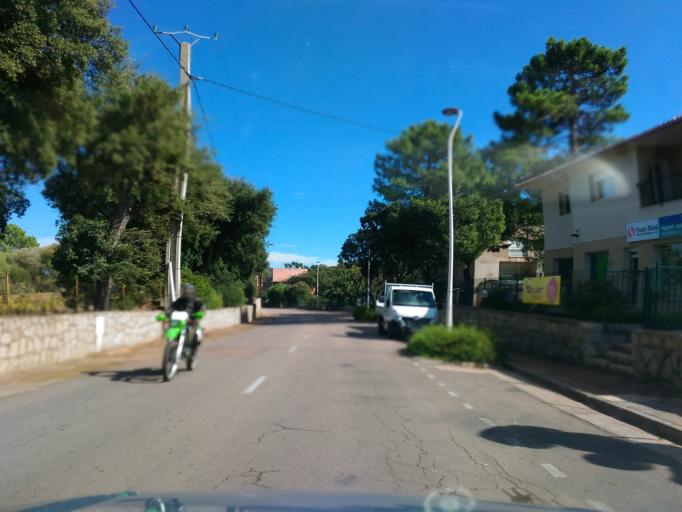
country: FR
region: Corsica
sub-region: Departement de la Corse-du-Sud
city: Porto-Vecchio
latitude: 41.6990
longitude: 9.3515
